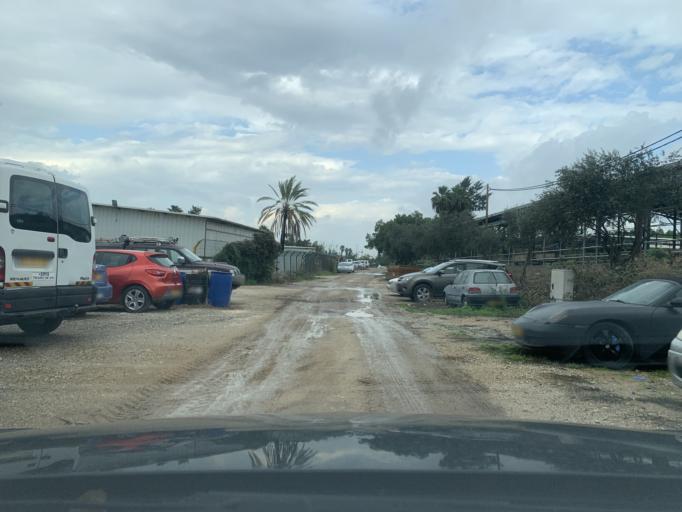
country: PS
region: West Bank
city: Qalqilyah
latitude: 32.2089
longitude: 34.9780
